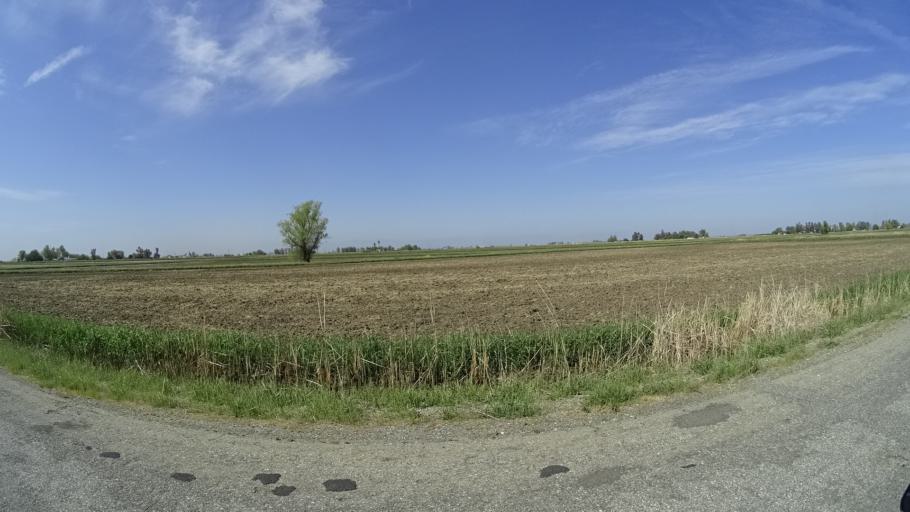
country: US
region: California
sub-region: Glenn County
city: Hamilton City
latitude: 39.5883
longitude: -122.0462
